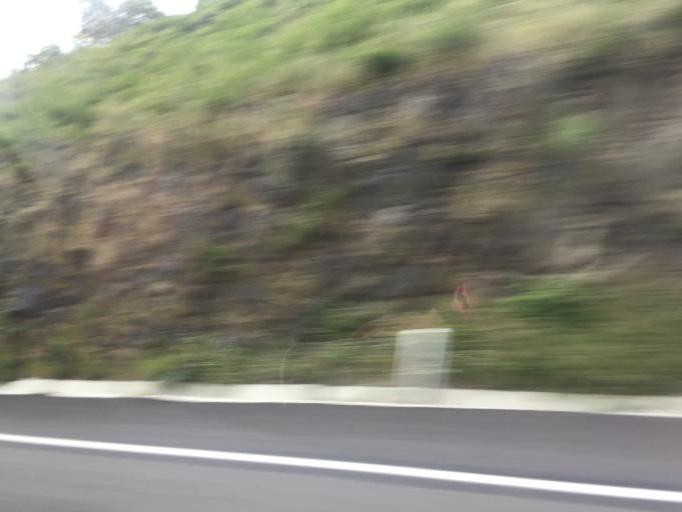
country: MX
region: Jalisco
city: Ocotlan
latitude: 20.4241
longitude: -102.7703
